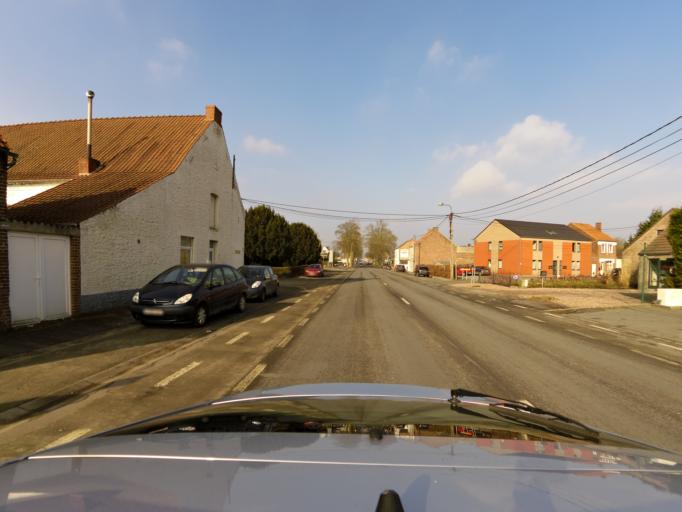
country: BE
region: Wallonia
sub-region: Province du Hainaut
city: Bernissart
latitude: 50.5175
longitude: 3.6674
